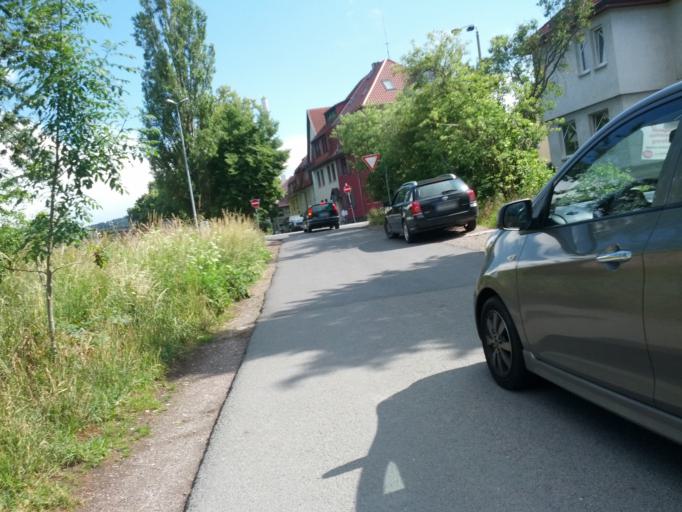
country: DE
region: Thuringia
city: Eisenach
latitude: 50.9784
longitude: 10.3408
